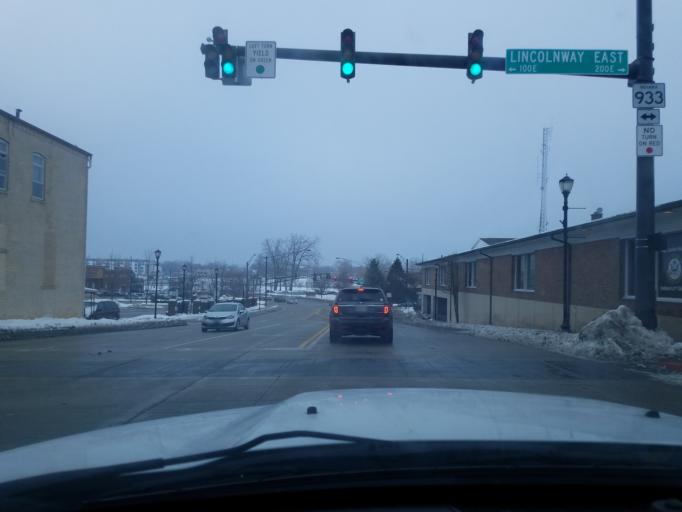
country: US
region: Indiana
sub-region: Saint Joseph County
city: Mishawaka
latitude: 41.6612
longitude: -86.1793
